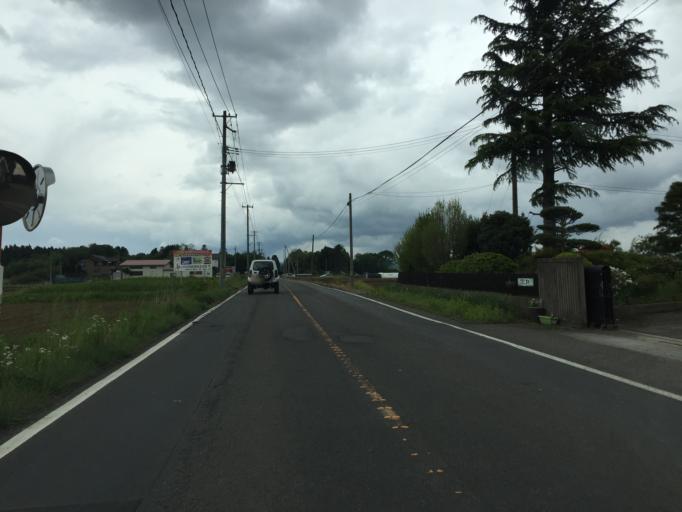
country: JP
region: Fukushima
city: Ishikawa
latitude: 37.1950
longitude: 140.3790
